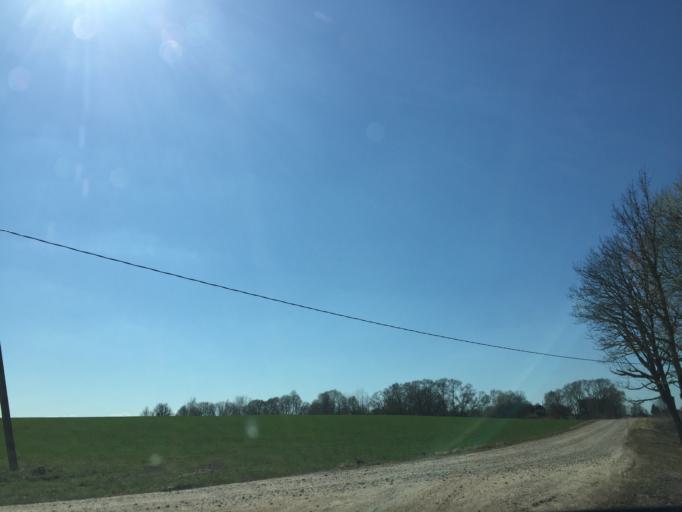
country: EE
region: Viljandimaa
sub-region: Viiratsi vald
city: Viiratsi
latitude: 58.3089
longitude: 25.6813
